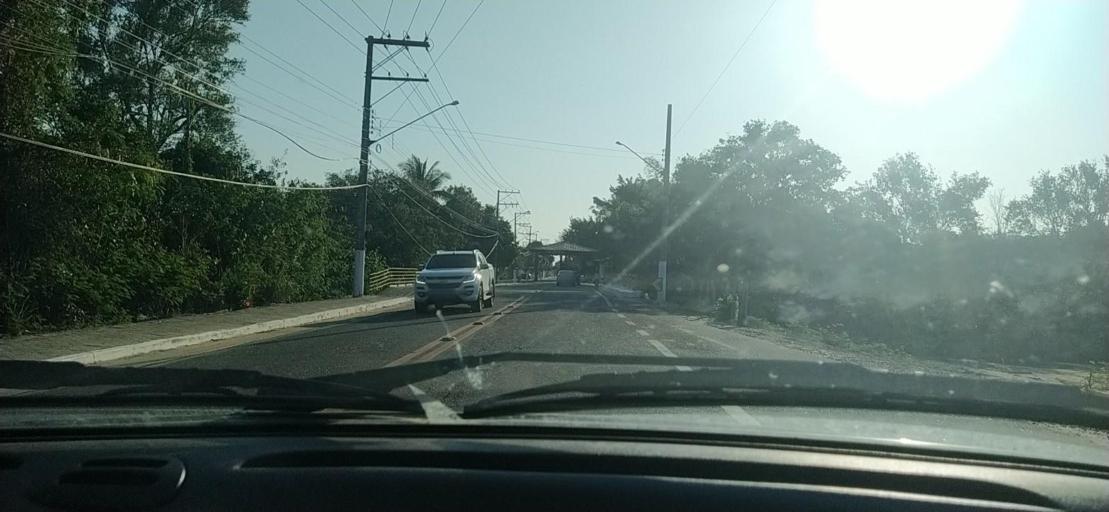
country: BR
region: Espirito Santo
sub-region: Conceicao Da Barra
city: Conceicao da Barra
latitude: -18.5671
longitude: -39.7463
